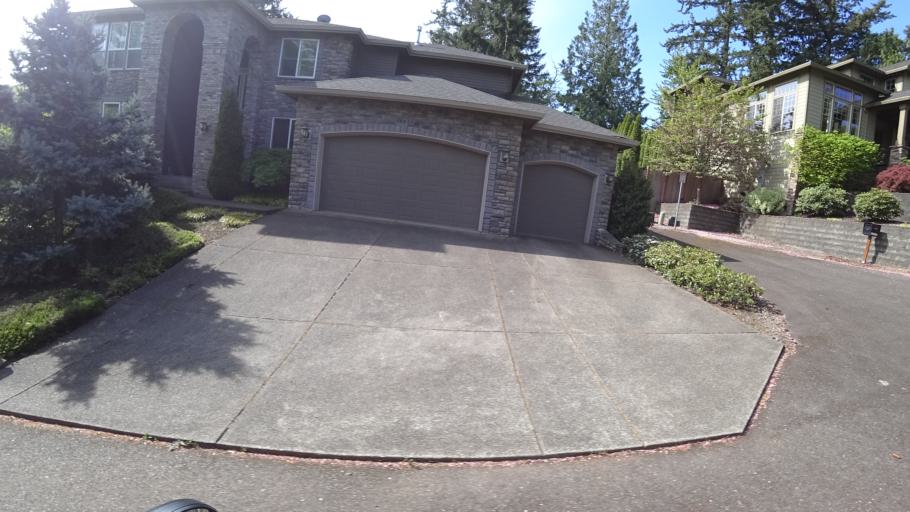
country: US
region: Oregon
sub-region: Washington County
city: Aloha
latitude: 45.4499
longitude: -122.8481
